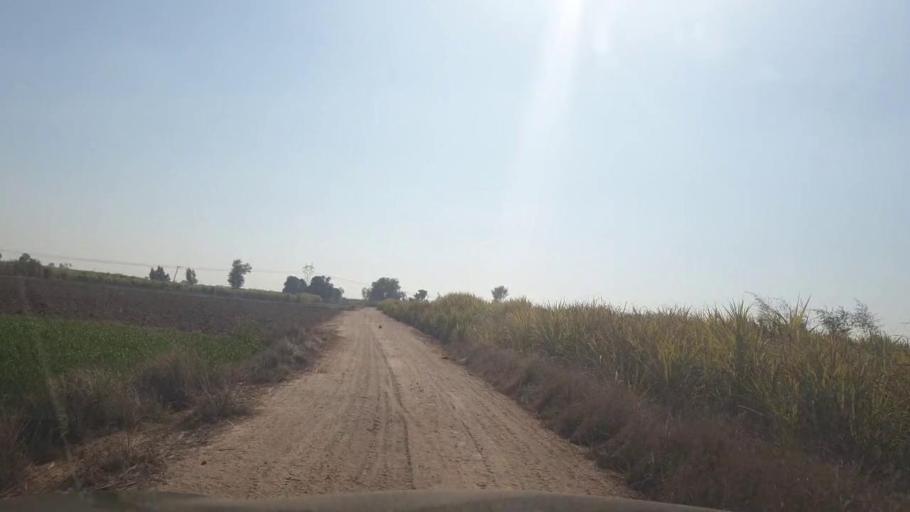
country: PK
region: Sindh
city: Adilpur
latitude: 27.9729
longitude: 69.4301
